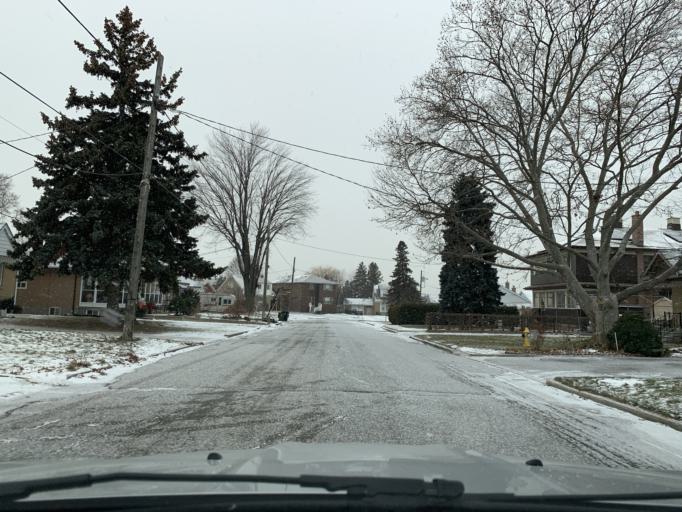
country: CA
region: Ontario
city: Concord
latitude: 43.7310
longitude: -79.4903
